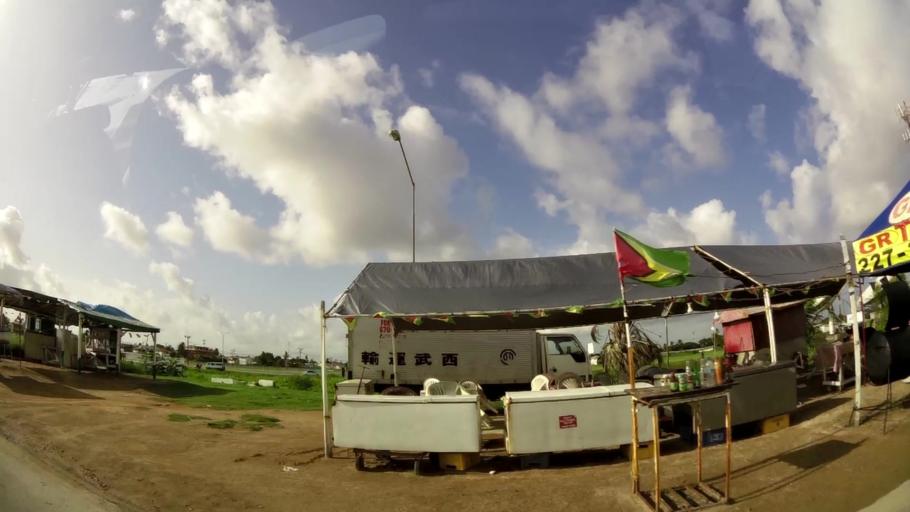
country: GY
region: Demerara-Mahaica
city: Georgetown
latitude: 6.8254
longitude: -58.1459
